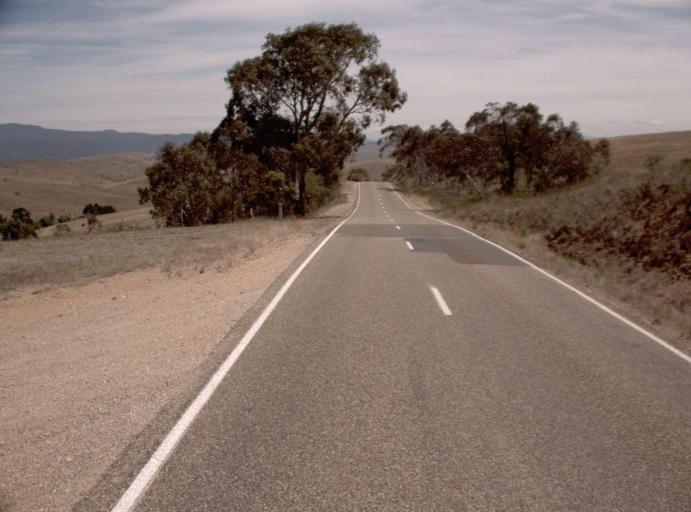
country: AU
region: Victoria
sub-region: Alpine
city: Mount Beauty
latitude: -37.0280
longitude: 147.6501
